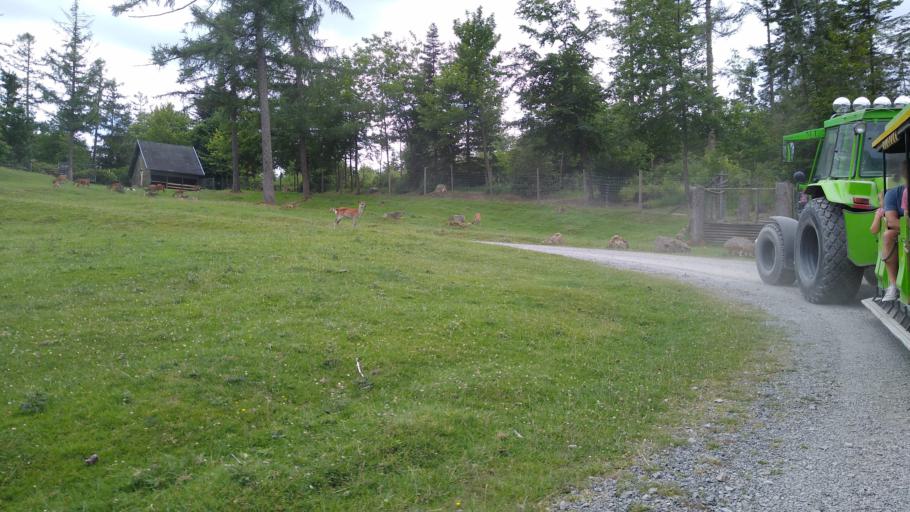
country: DE
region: North Rhine-Westphalia
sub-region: Regierungsbezirk Arnsberg
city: Kirchhundem
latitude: 51.0680
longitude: 8.1795
